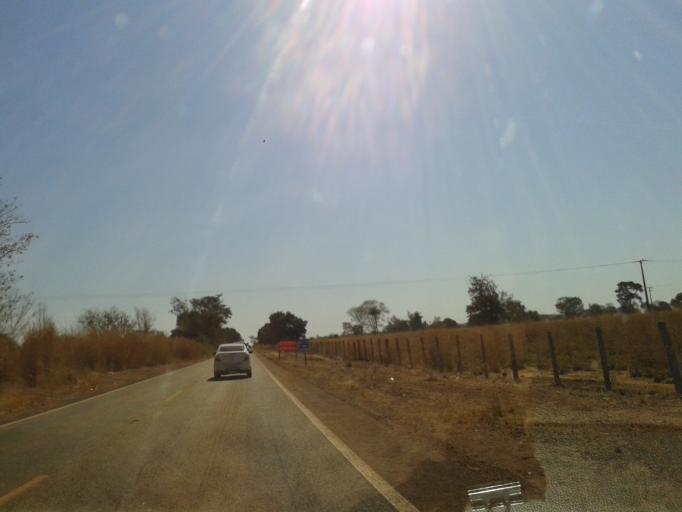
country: BR
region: Goias
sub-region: Crixas
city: Crixas
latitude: -14.1267
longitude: -50.3496
